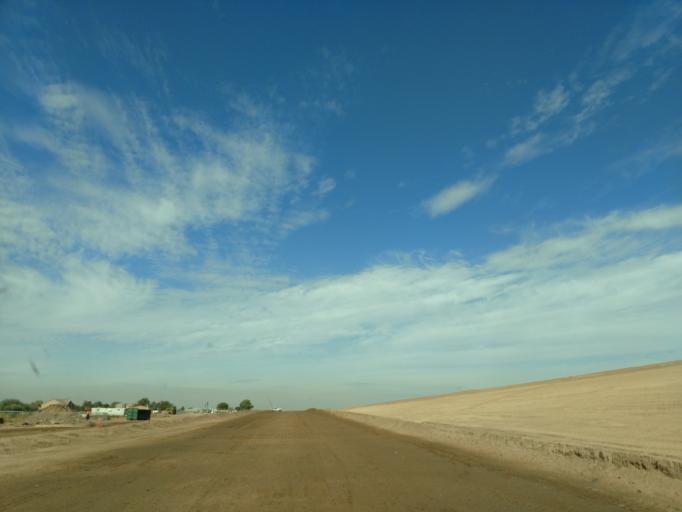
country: US
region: Arizona
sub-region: Maricopa County
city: Laveen
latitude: 33.3787
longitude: -112.1904
